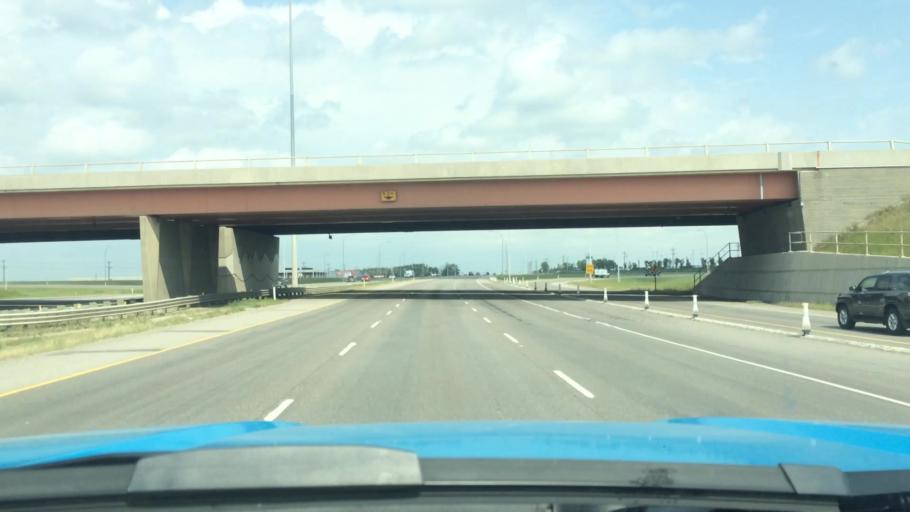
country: CA
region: Alberta
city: Airdrie
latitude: 51.2994
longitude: -114.0015
